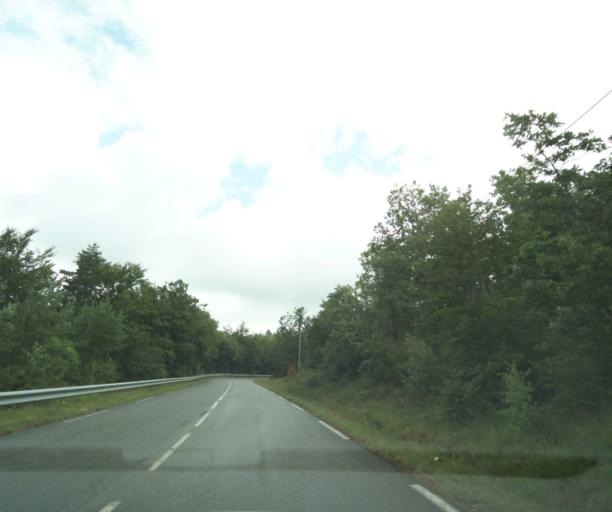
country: FR
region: Languedoc-Roussillon
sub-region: Departement de la Lozere
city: La Canourgue
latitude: 44.4031
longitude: 3.1427
